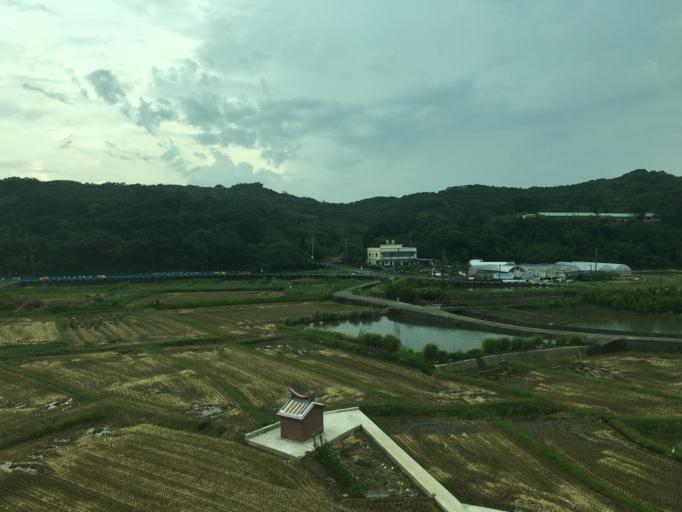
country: TW
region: Taiwan
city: Taoyuan City
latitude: 25.0805
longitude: 121.3001
